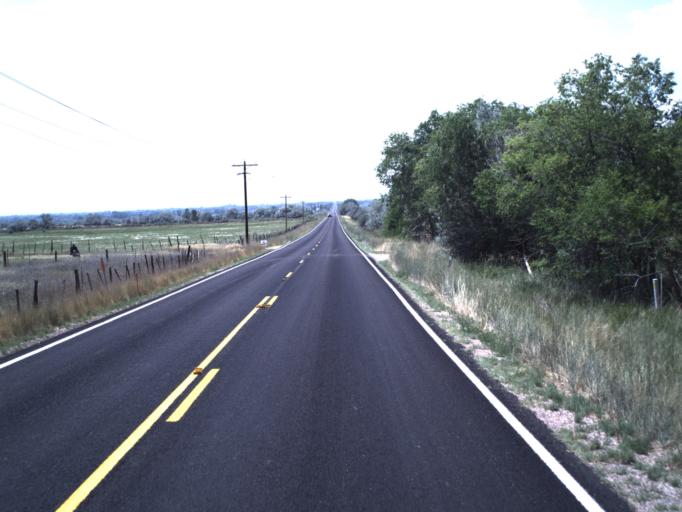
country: US
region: Utah
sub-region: Duchesne County
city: Roosevelt
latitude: 40.4037
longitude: -109.8252
